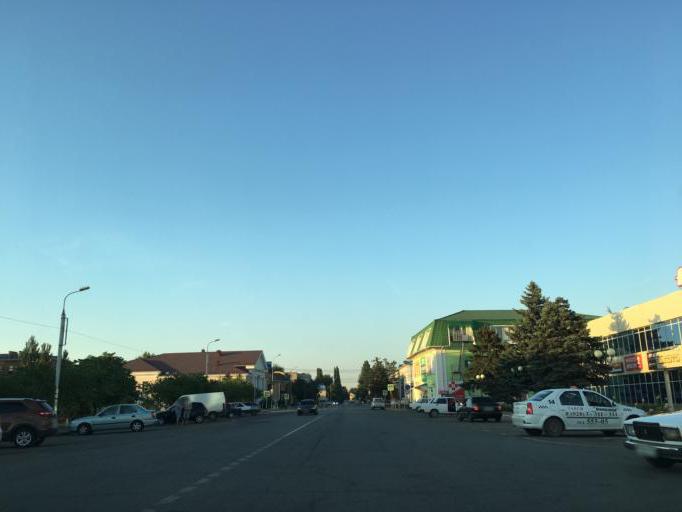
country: RU
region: Krasnodarskiy
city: Kushchevskaya
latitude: 46.5650
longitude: 39.6276
